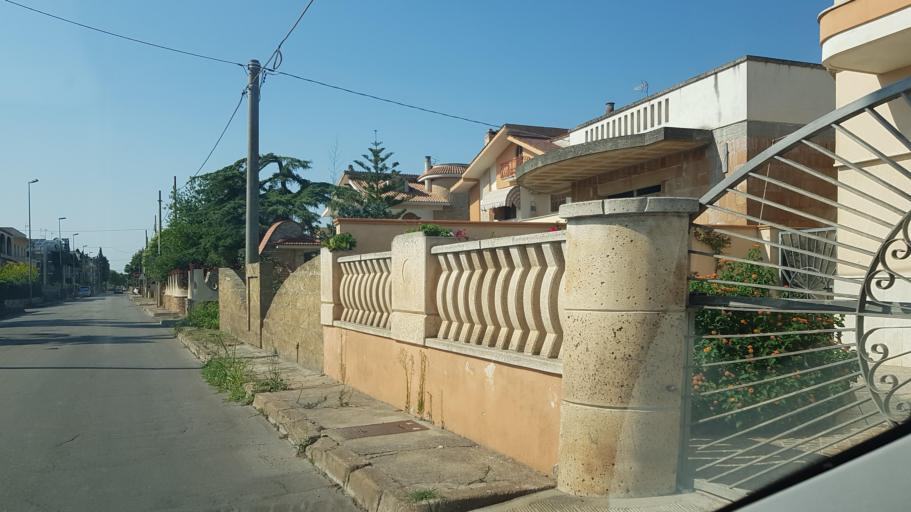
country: IT
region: Apulia
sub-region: Provincia di Lecce
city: Taurisano
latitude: 39.9490
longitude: 18.2189
